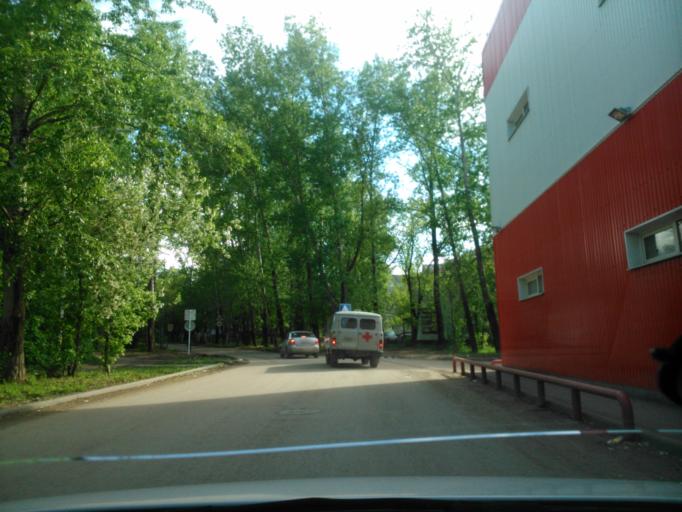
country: RU
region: Perm
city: Lobanovo
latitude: 57.8652
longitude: 56.2890
